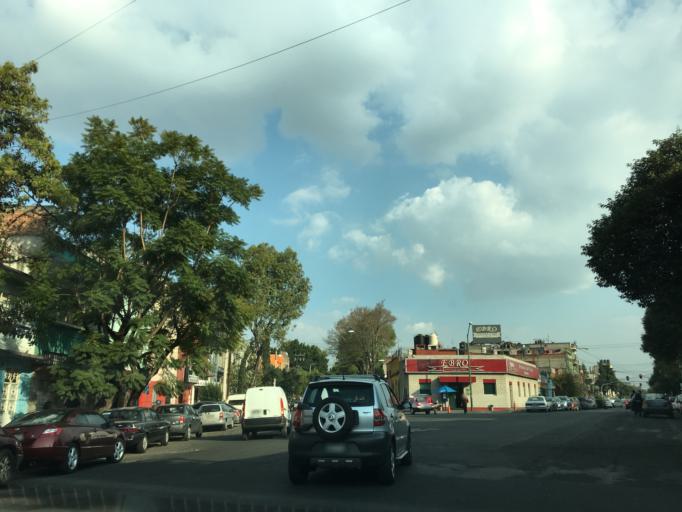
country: MX
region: Mexico City
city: Mexico City
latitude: 19.4176
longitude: -99.1424
